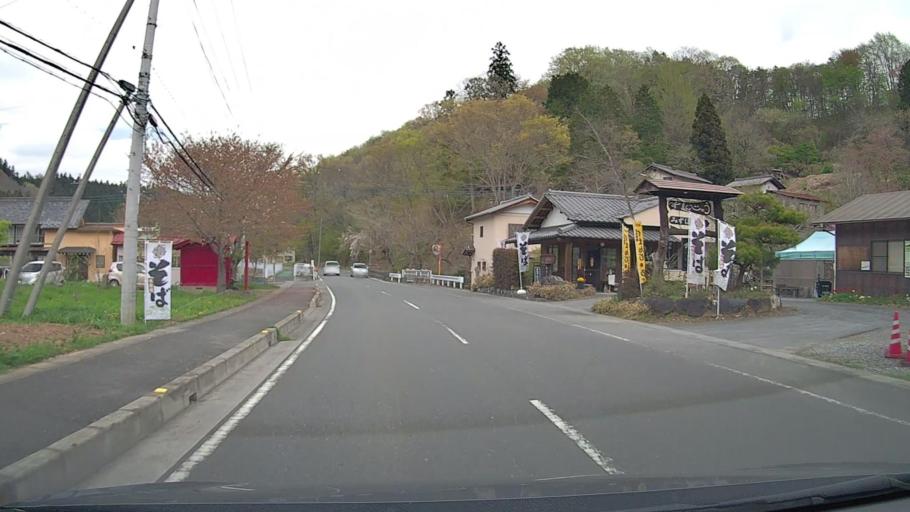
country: JP
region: Saitama
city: Yorii
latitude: 36.0594
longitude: 139.1307
